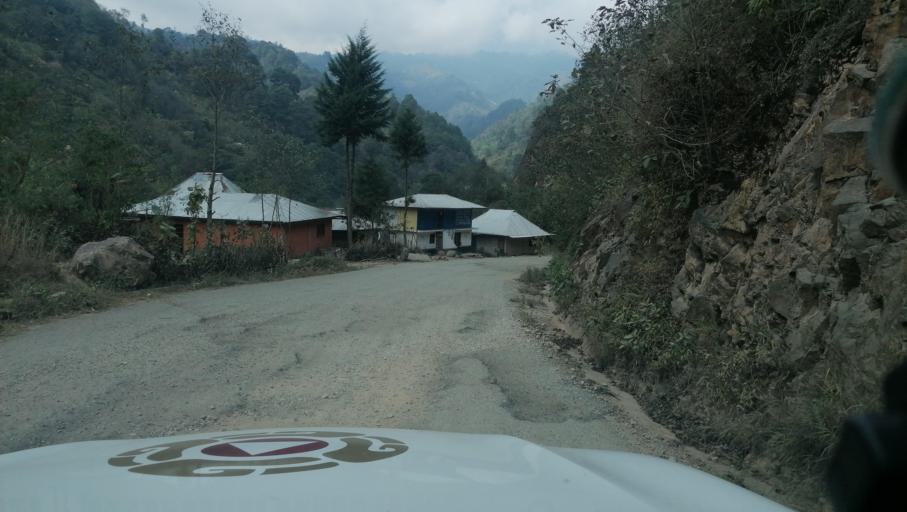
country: GT
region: San Marcos
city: Tacana
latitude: 15.2154
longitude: -92.2023
